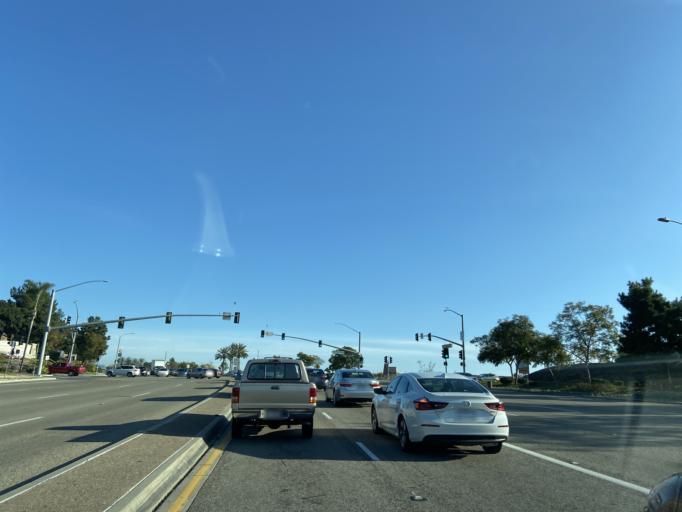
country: US
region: California
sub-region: San Diego County
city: Bonita
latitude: 32.6292
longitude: -116.9680
